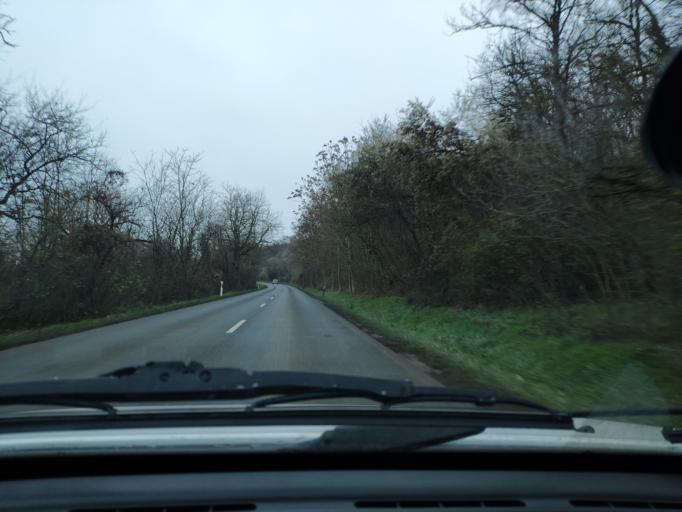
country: HU
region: Pest
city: Biatorbagy
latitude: 47.4531
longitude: 18.8187
